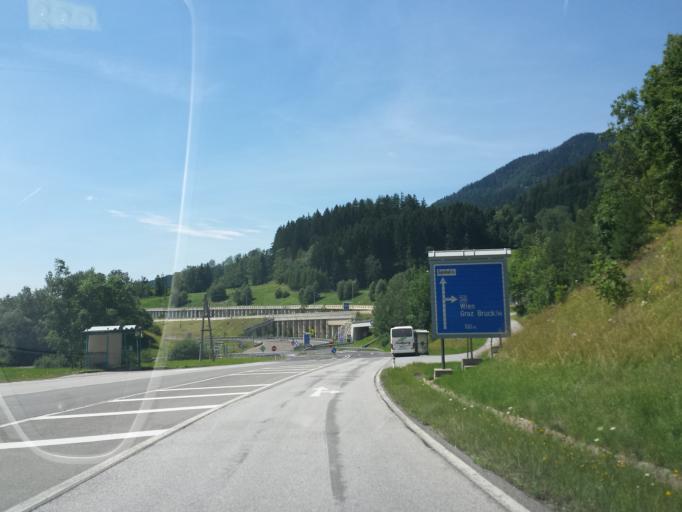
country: AT
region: Styria
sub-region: Politischer Bezirk Bruck-Muerzzuschlag
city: Spital am Semmering
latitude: 47.6205
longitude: 15.7804
